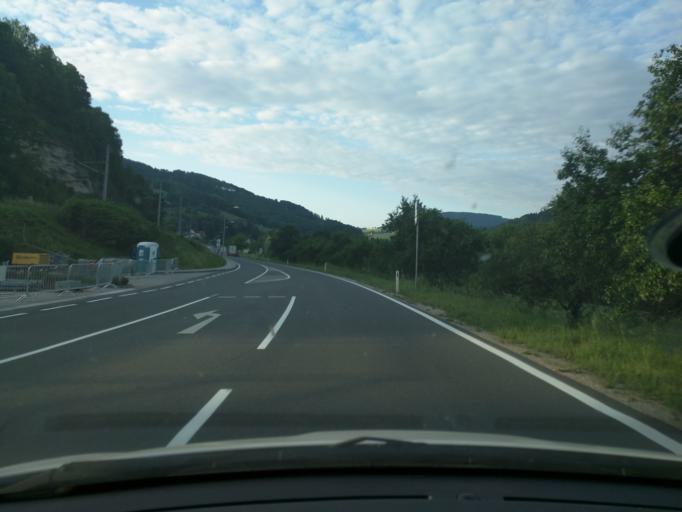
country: AT
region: Lower Austria
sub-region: Politischer Bezirk Amstetten
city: Sonntagberg
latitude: 48.0051
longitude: 14.7350
